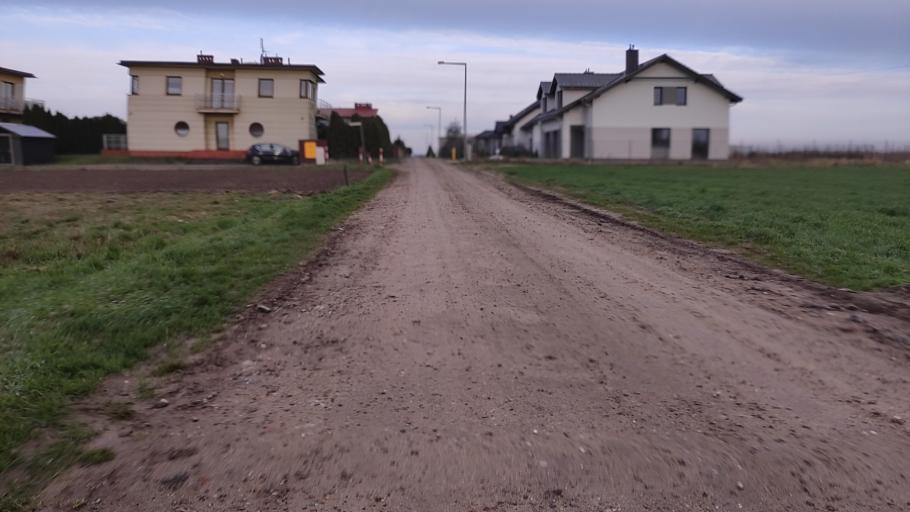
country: PL
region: Greater Poland Voivodeship
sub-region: Powiat poznanski
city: Kleszczewo
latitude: 52.4006
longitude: 17.1551
